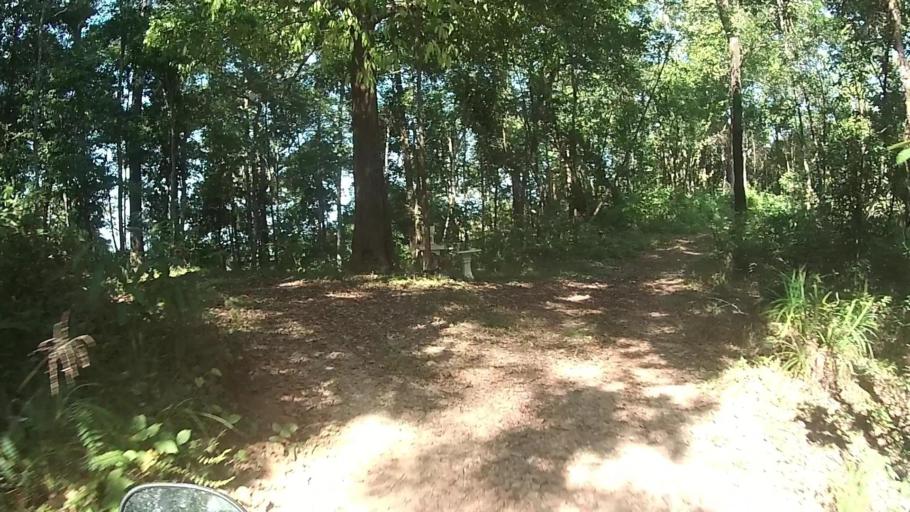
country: TH
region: Chiang Mai
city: Mae On
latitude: 19.0406
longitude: 99.2898
